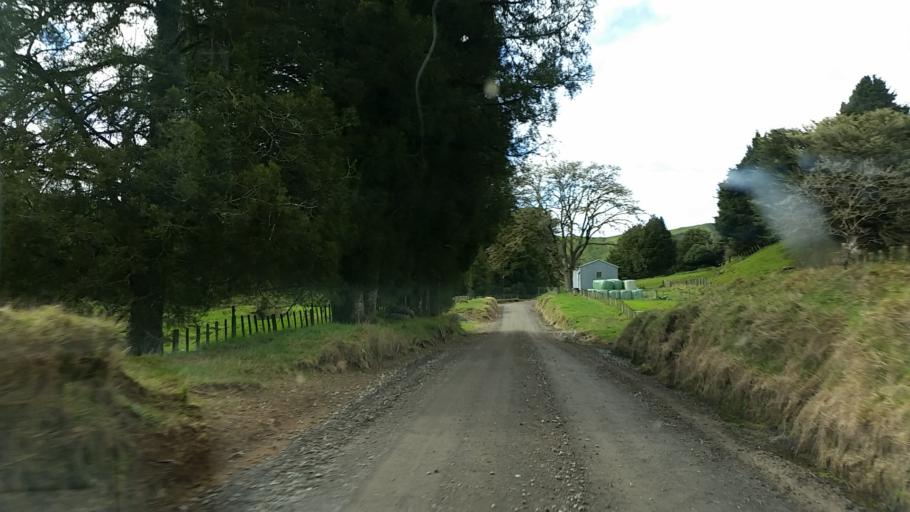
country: NZ
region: Taranaki
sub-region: New Plymouth District
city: Waitara
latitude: -39.1619
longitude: 174.5848
